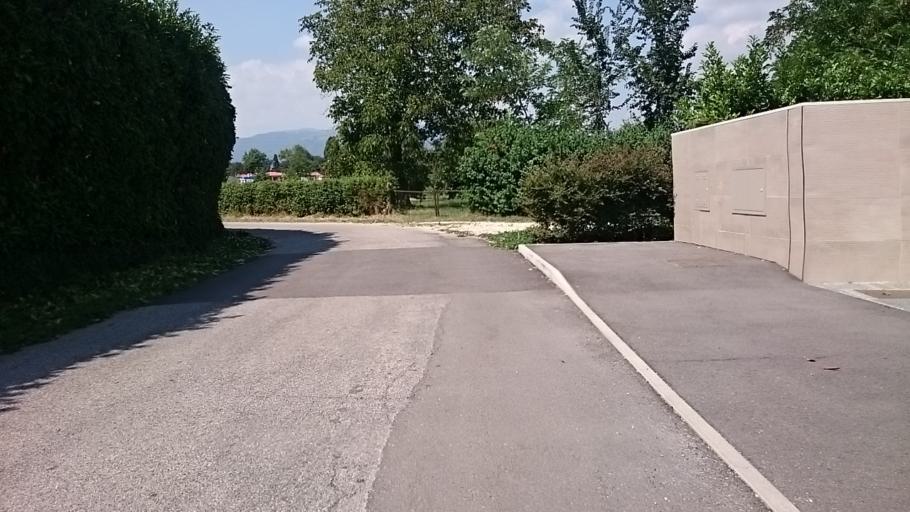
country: IT
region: Veneto
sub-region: Provincia di Vicenza
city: Rosa
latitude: 45.7240
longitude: 11.7361
